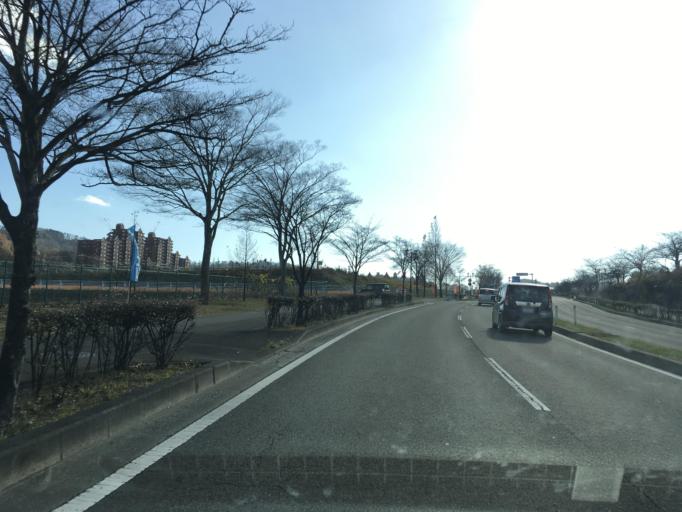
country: JP
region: Miyagi
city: Sendai
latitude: 38.2620
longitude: 140.7631
